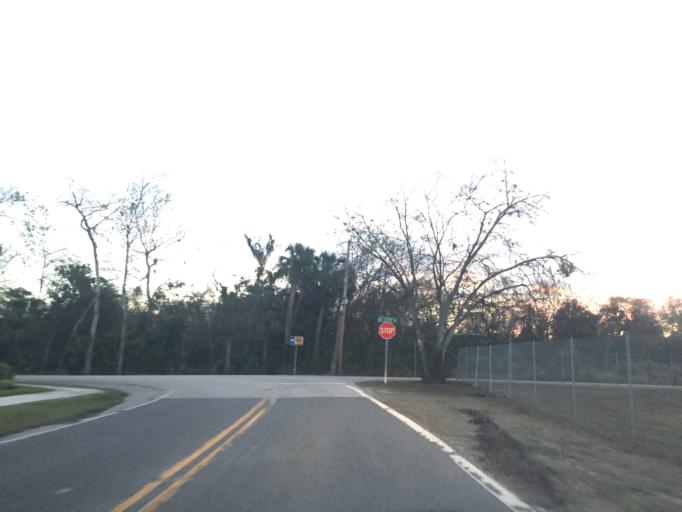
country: US
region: Florida
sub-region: Seminole County
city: Oviedo
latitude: 28.6903
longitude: -81.2092
